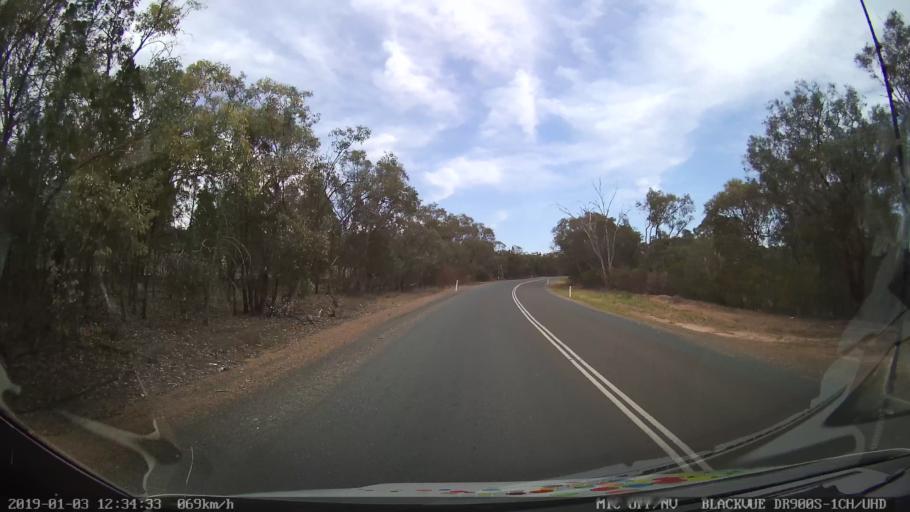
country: AU
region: New South Wales
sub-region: Weddin
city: Grenfell
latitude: -33.8754
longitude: 148.1663
